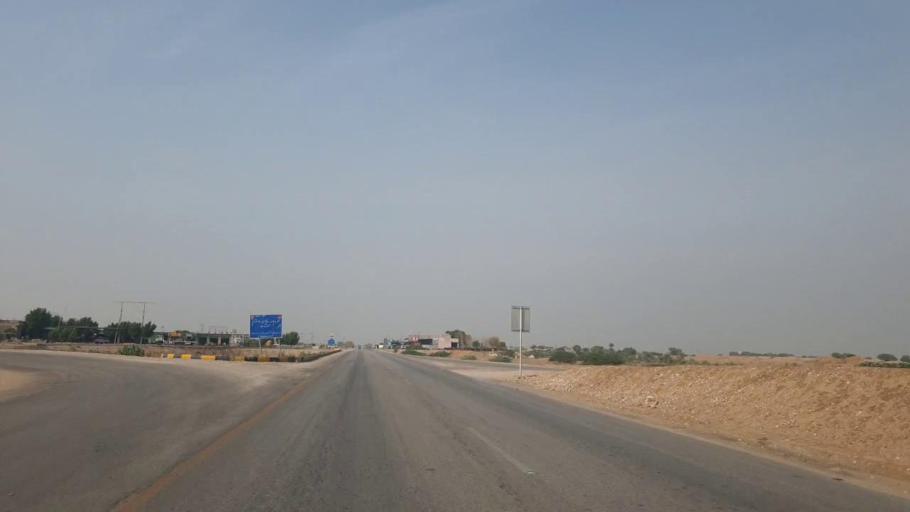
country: PK
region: Sindh
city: Sann
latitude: 26.1569
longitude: 68.0230
